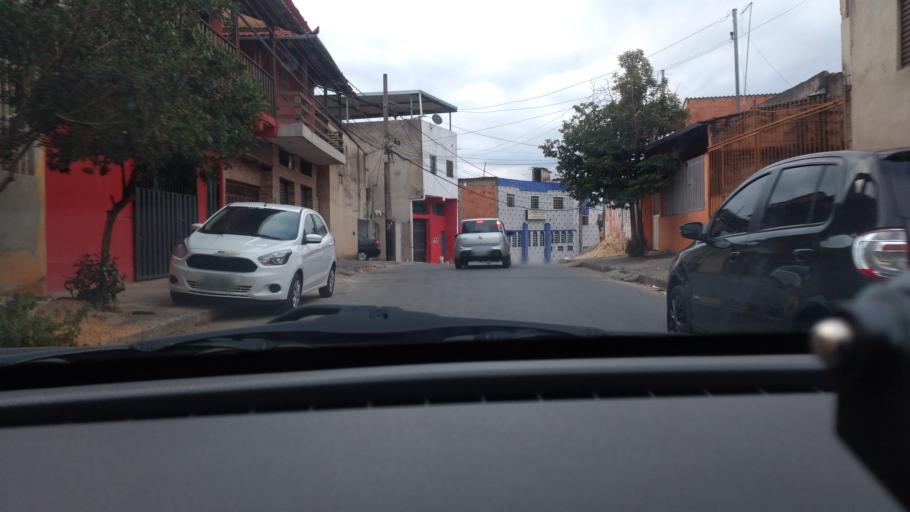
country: BR
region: Minas Gerais
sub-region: Santa Luzia
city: Santa Luzia
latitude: -19.8148
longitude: -43.9387
